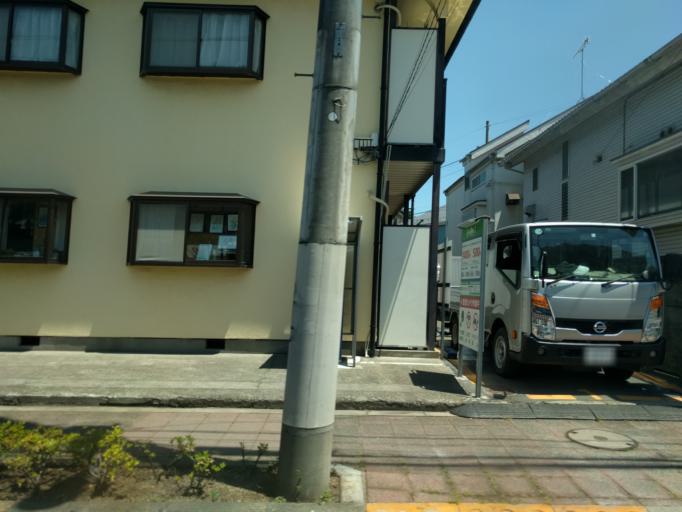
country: JP
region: Tokyo
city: Mitaka-shi
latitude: 35.6598
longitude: 139.6031
